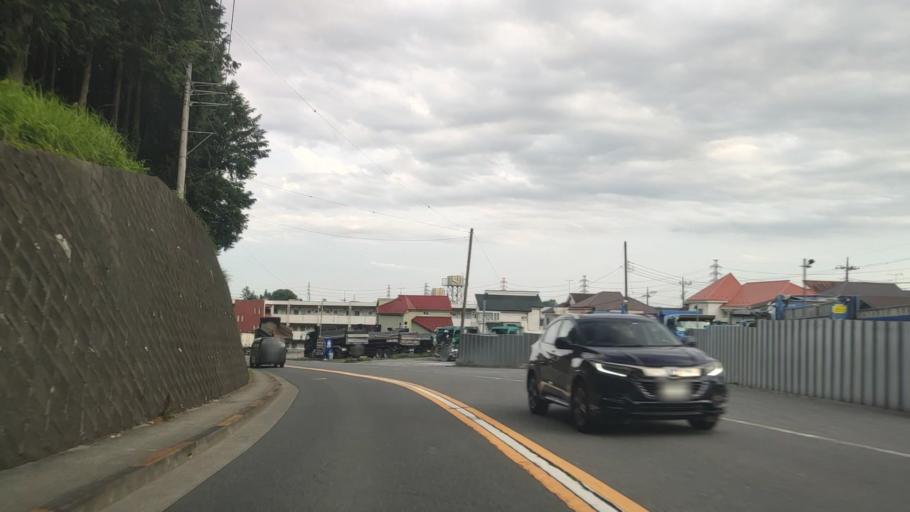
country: JP
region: Saitama
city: Hanno
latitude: 35.8101
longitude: 139.3004
